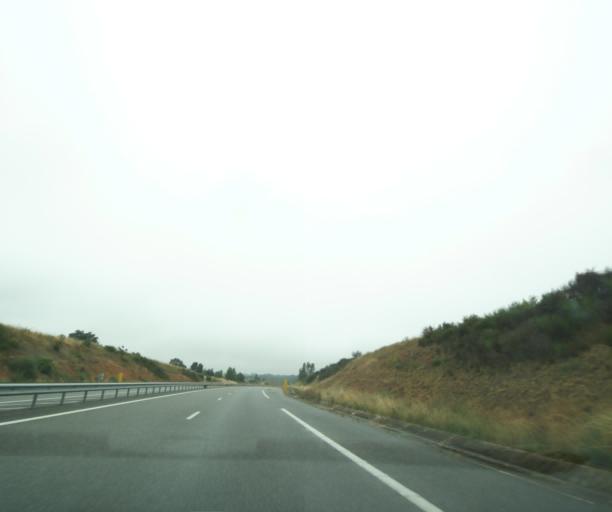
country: FR
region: Midi-Pyrenees
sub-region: Departement du Tarn
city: Carmaux
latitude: 44.0606
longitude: 2.2148
